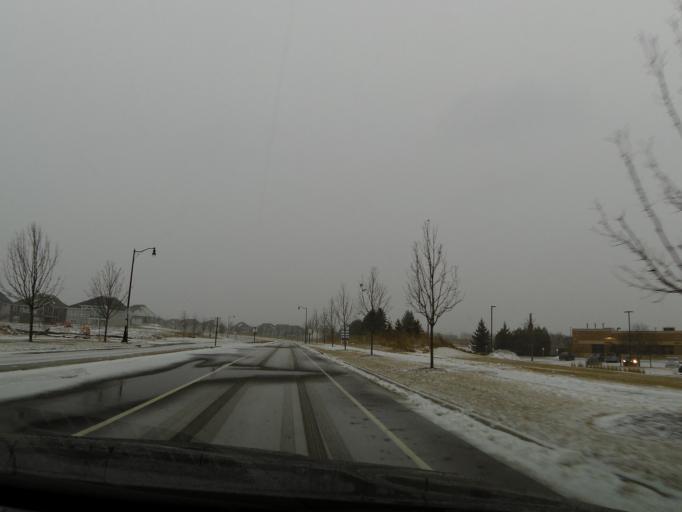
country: US
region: Minnesota
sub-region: Washington County
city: Oakdale
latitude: 44.9559
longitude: -92.9238
